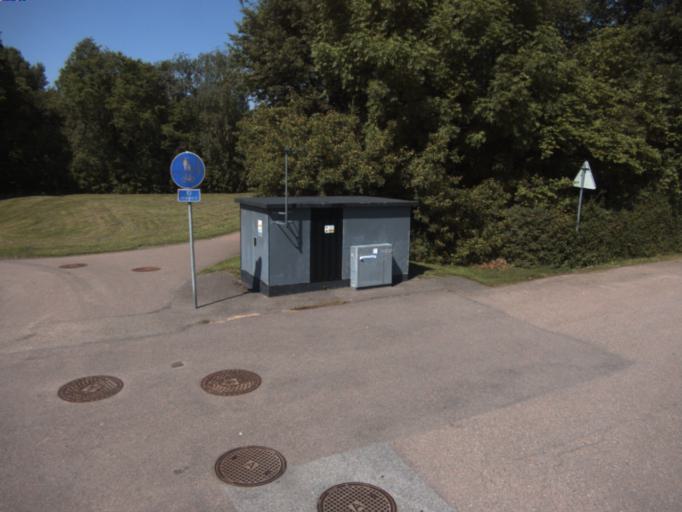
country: SE
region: Skane
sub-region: Helsingborg
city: Barslov
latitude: 56.0315
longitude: 12.8200
